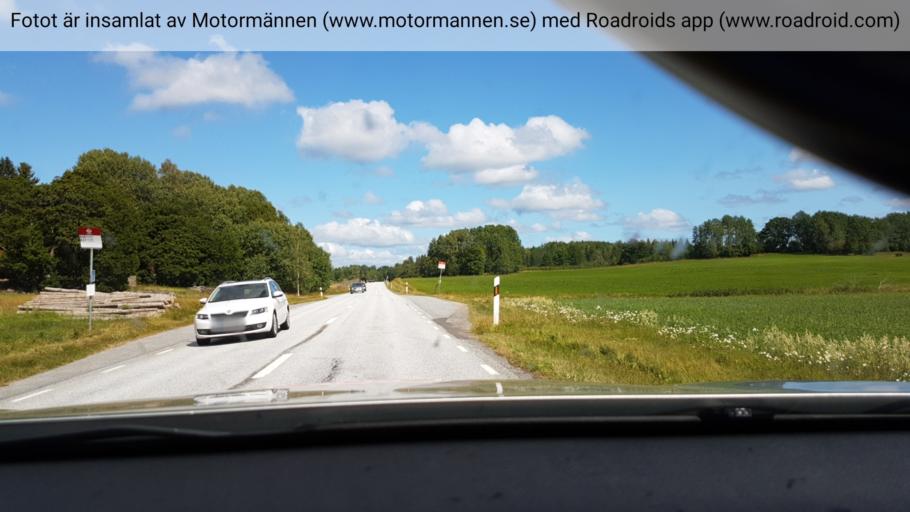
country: SE
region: Stockholm
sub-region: Norrtalje Kommun
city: Norrtalje
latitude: 59.9080
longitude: 18.7047
